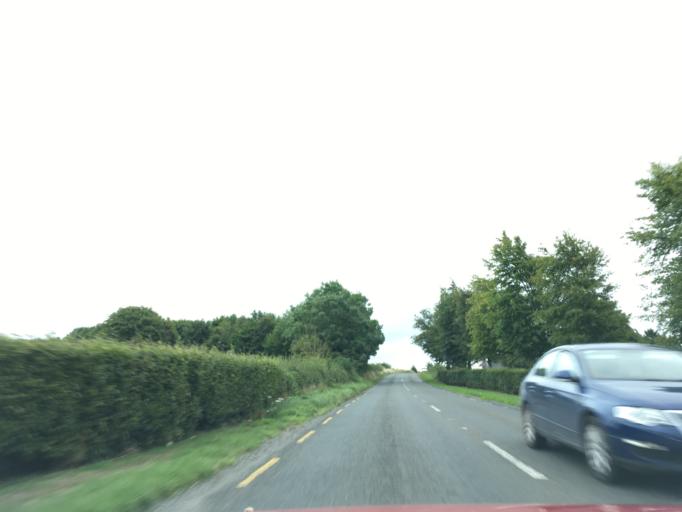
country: IE
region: Munster
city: Cashel
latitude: 52.4610
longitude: -7.8254
